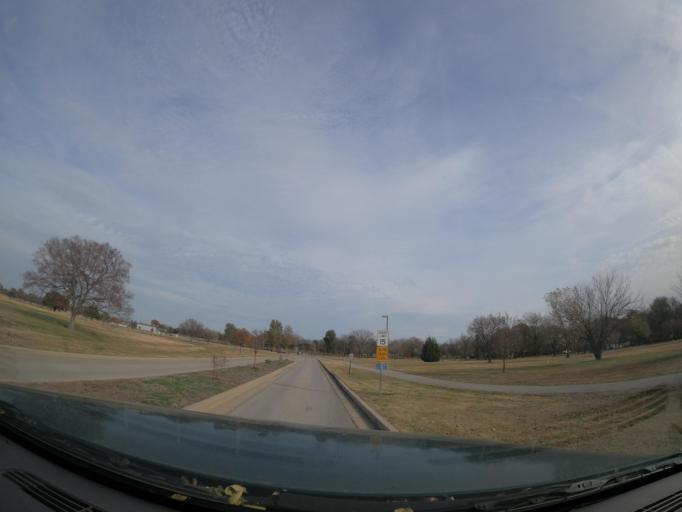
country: US
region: Oklahoma
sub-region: Tulsa County
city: Turley
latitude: 36.2435
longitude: -95.9582
